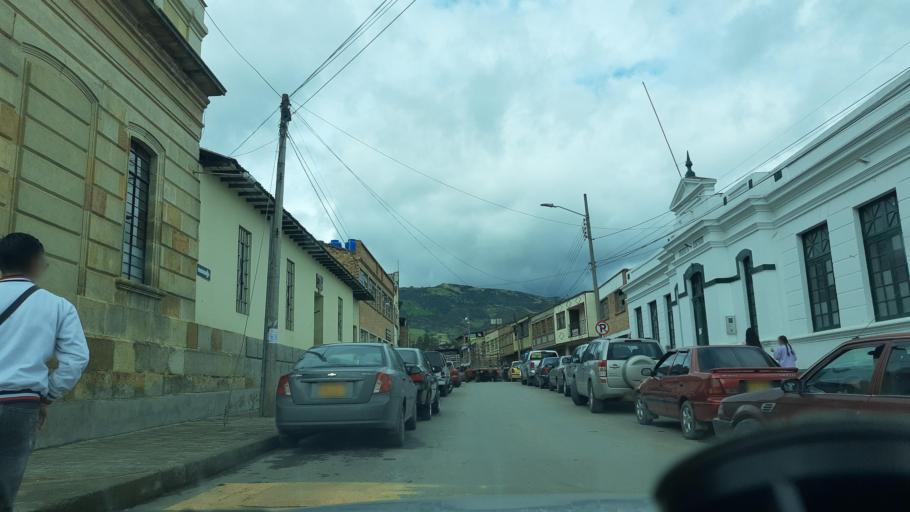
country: CO
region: Cundinamarca
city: Villapinzon
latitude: 5.2157
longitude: -73.5963
